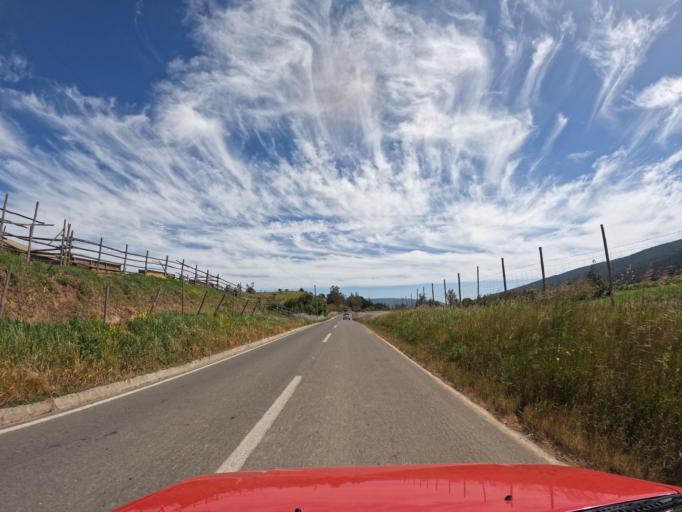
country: CL
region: Maule
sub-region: Provincia de Talca
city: Constitucion
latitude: -35.0081
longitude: -72.0332
